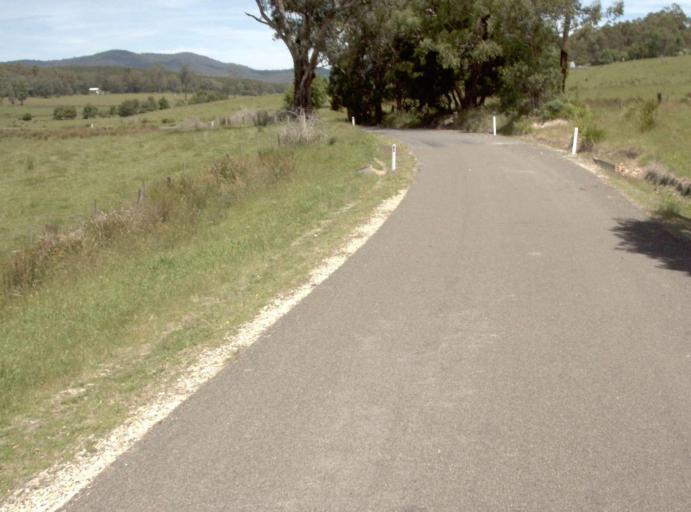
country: AU
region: New South Wales
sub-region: Bombala
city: Bombala
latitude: -37.3886
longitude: 149.0126
